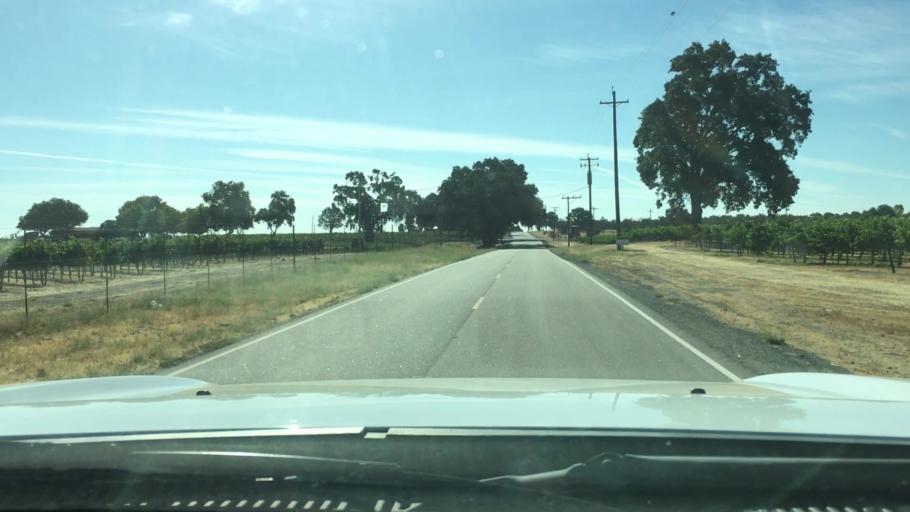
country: US
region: California
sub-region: San Luis Obispo County
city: Atascadero
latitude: 35.5535
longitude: -120.6145
